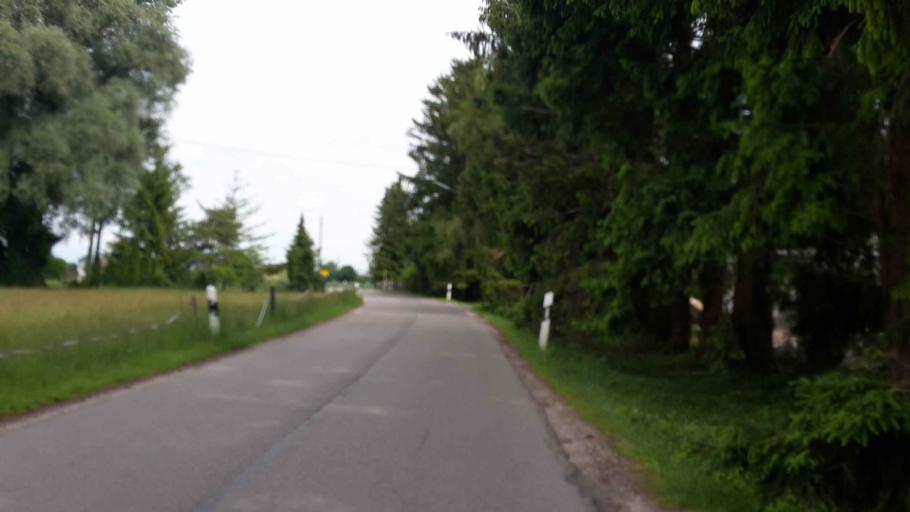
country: DE
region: Bavaria
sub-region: Upper Bavaria
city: Karlsfeld
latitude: 48.2191
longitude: 11.4266
